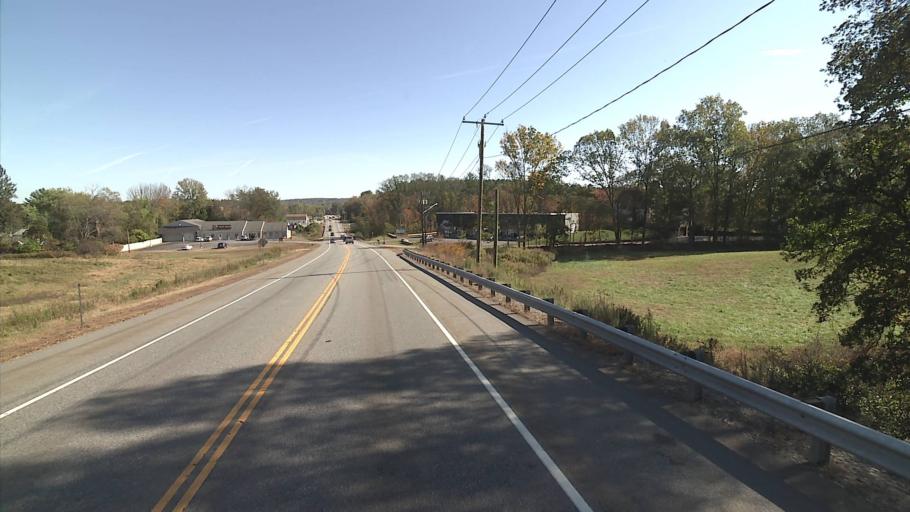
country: US
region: Connecticut
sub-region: Windham County
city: East Brooklyn
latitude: 41.7963
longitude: -71.9197
